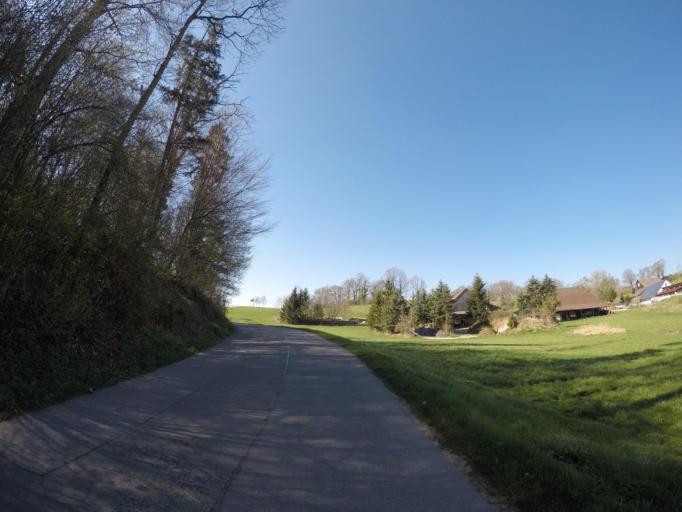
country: DE
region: Baden-Wuerttemberg
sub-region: Tuebingen Region
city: Ebenweiler
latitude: 47.8764
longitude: 9.5088
